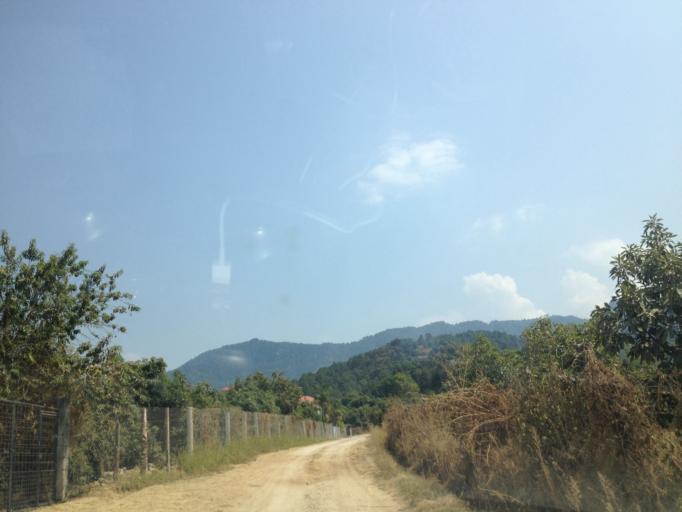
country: MX
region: Michoacan
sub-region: Zitacuaro
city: Macutzio
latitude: 19.4948
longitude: -100.3309
